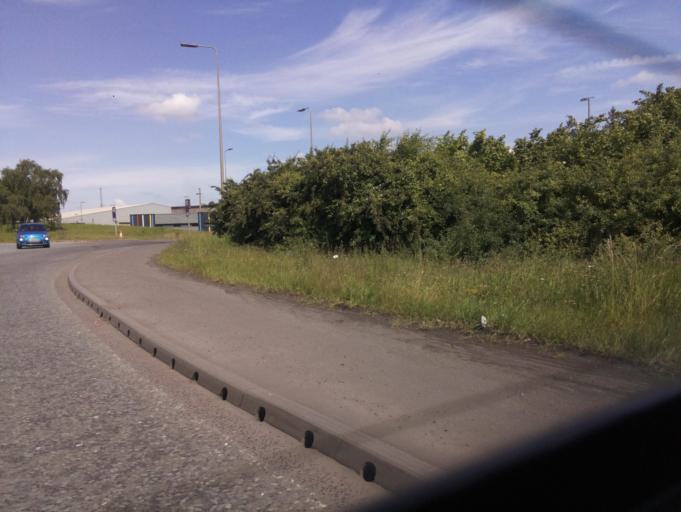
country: GB
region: England
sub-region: North Lincolnshire
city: Bottesford
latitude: 53.5644
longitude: -0.6071
